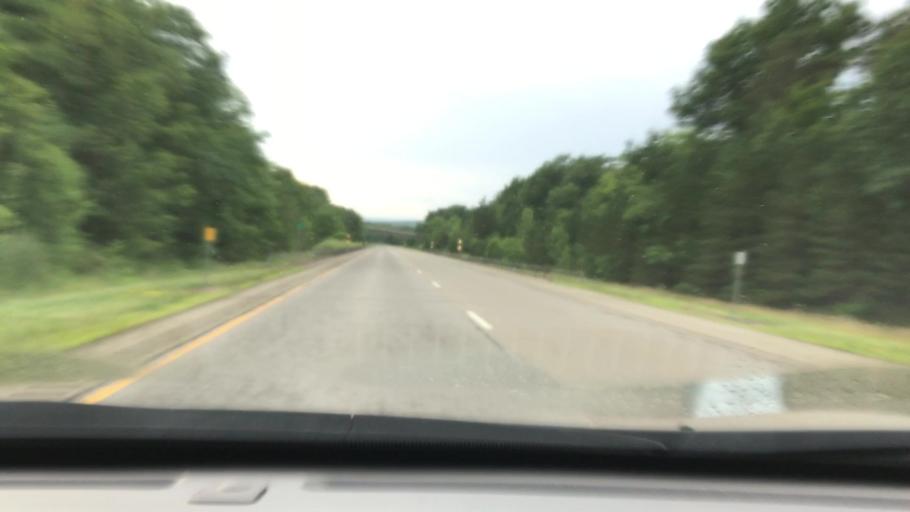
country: US
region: New York
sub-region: Erie County
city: North Boston
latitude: 42.6495
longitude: -78.7645
